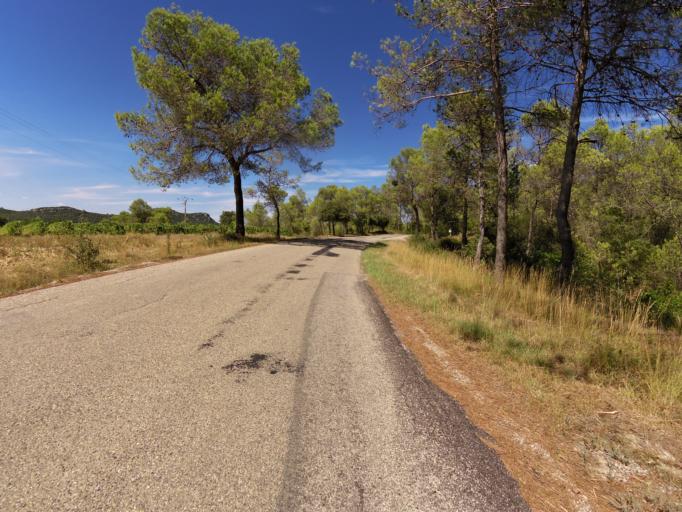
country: FR
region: Languedoc-Roussillon
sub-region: Departement du Gard
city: Quissac
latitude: 43.9117
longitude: 4.0473
